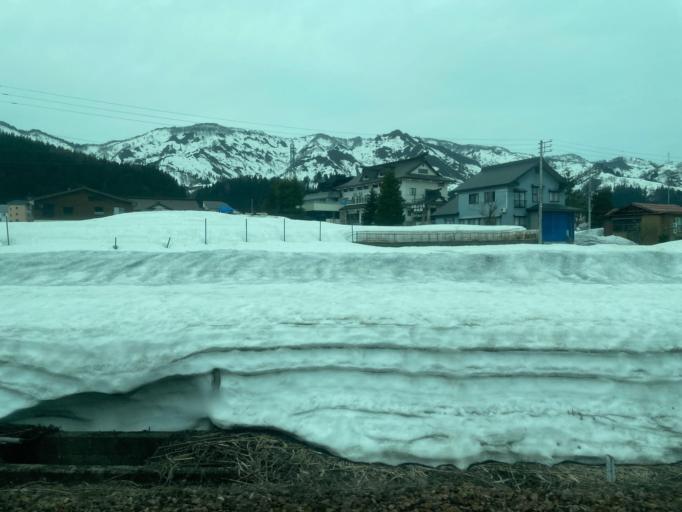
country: JP
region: Niigata
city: Shiozawa
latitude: 36.9839
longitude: 138.8026
